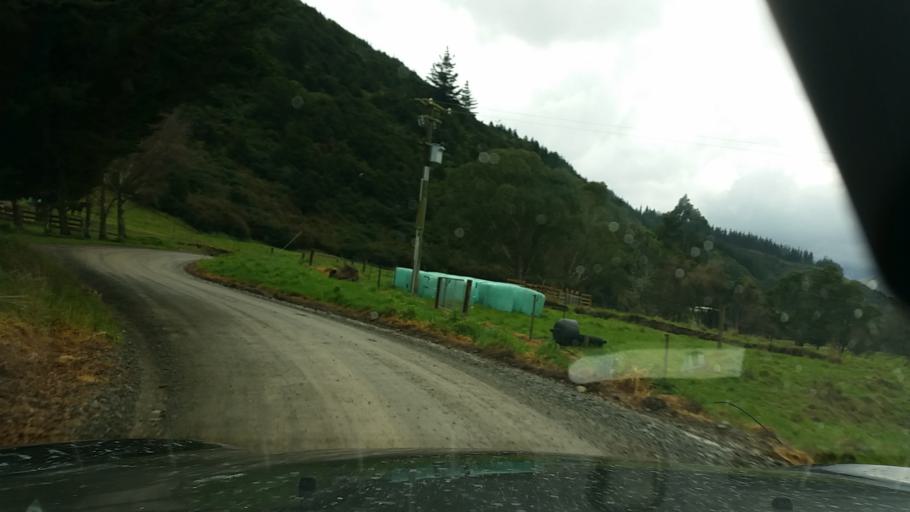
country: NZ
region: Marlborough
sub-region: Marlborough District
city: Picton
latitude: -41.3039
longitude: 173.6635
